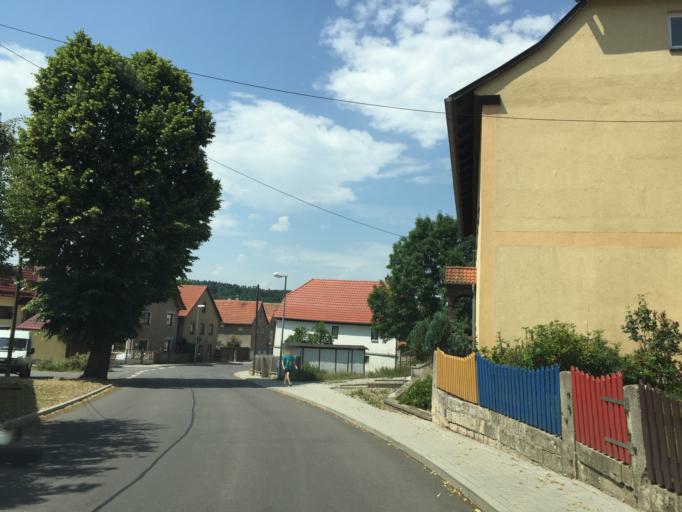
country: DE
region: Thuringia
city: Barchfeld
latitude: 50.8007
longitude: 11.1707
